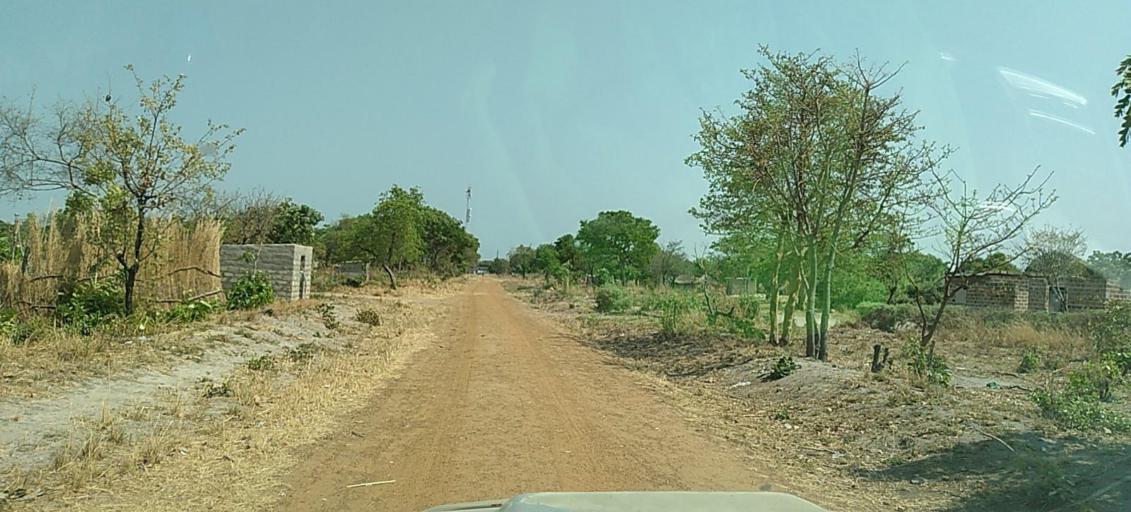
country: ZM
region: North-Western
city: Kalengwa
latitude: -13.2324
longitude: 24.7506
